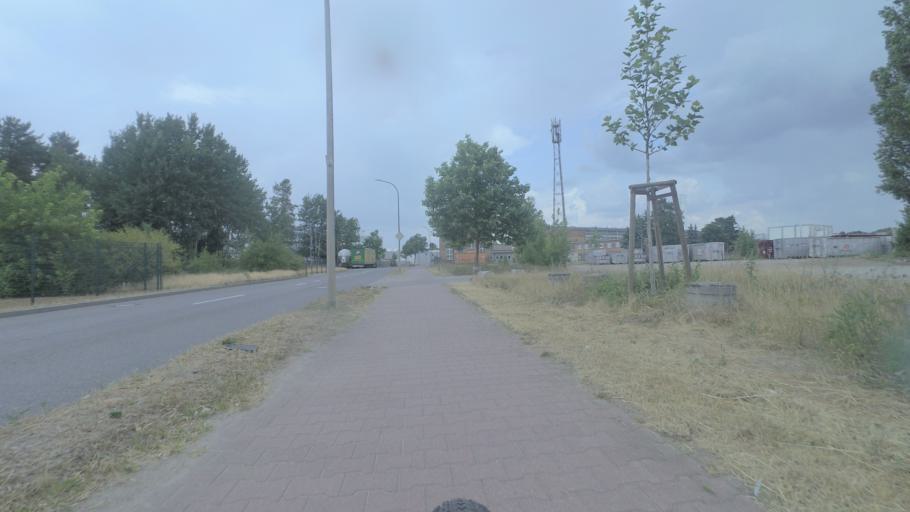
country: DE
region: Brandenburg
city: Ludwigsfelde
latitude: 52.3240
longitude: 13.2591
